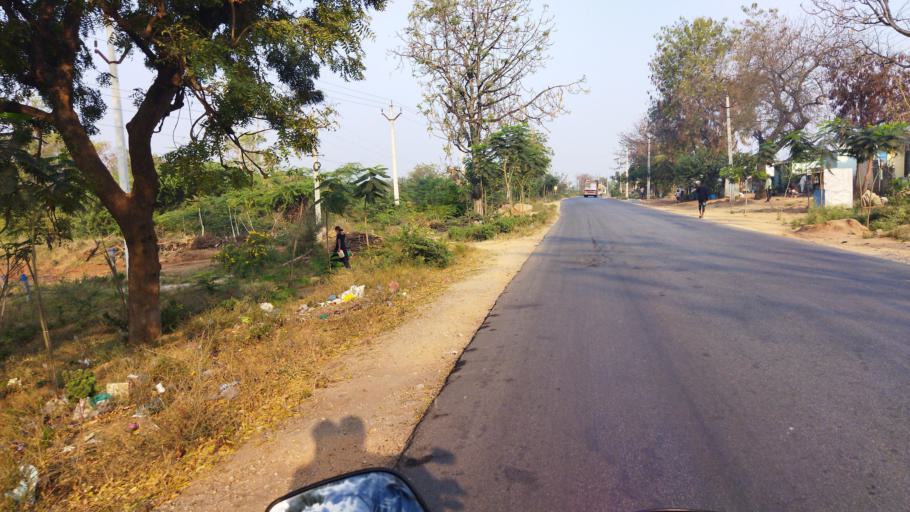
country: IN
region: Telangana
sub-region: Nalgonda
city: Nalgonda
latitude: 17.2402
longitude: 79.1164
